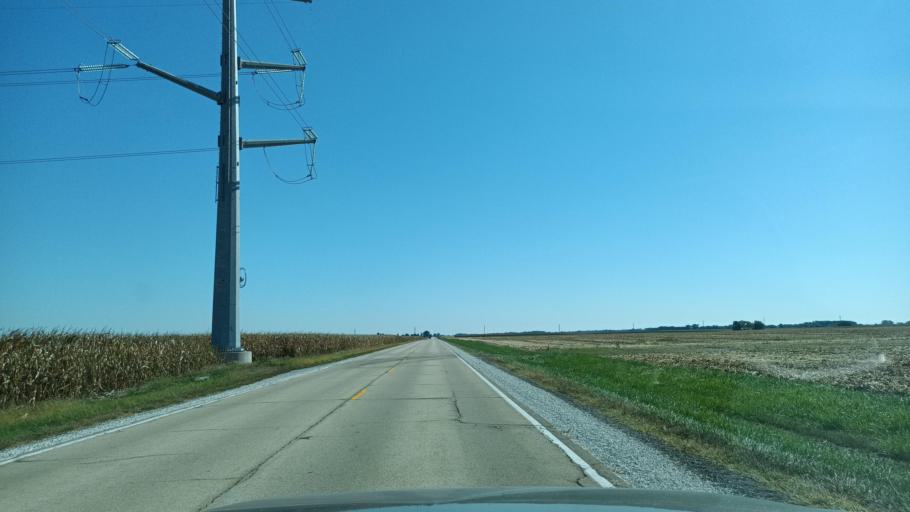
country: US
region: Illinois
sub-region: Peoria County
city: Elmwood
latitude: 40.9022
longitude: -89.9762
